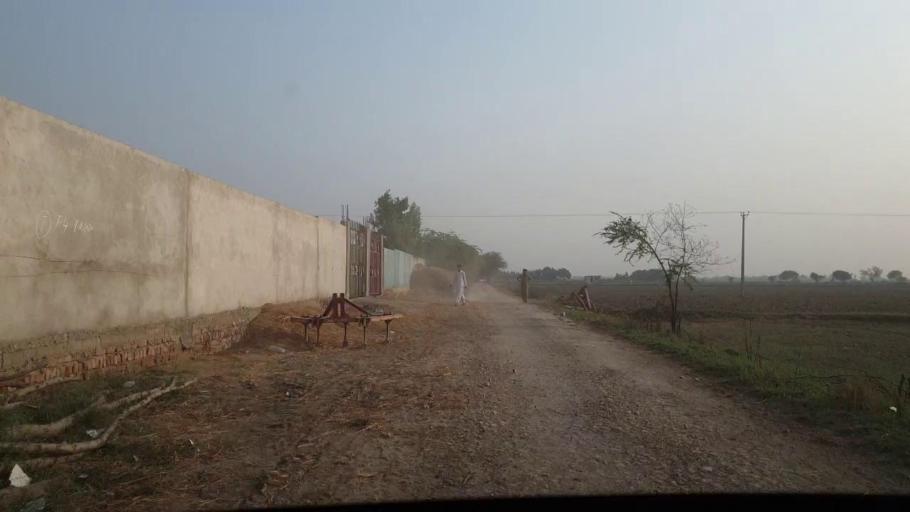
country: PK
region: Sindh
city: Chuhar Jamali
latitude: 24.2560
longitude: 68.1133
